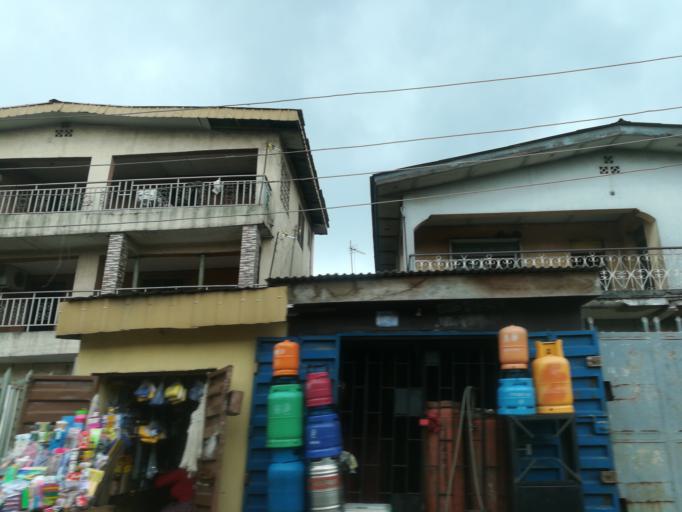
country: NG
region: Lagos
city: Oshodi
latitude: 6.5519
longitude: 3.3393
